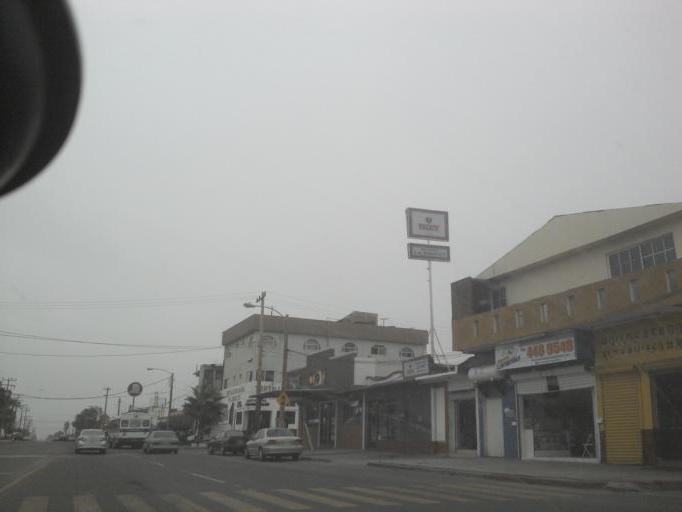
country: MX
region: Baja California
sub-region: Tijuana
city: La Esperanza [Granjas Familiares]
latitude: 32.5119
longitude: -117.1200
